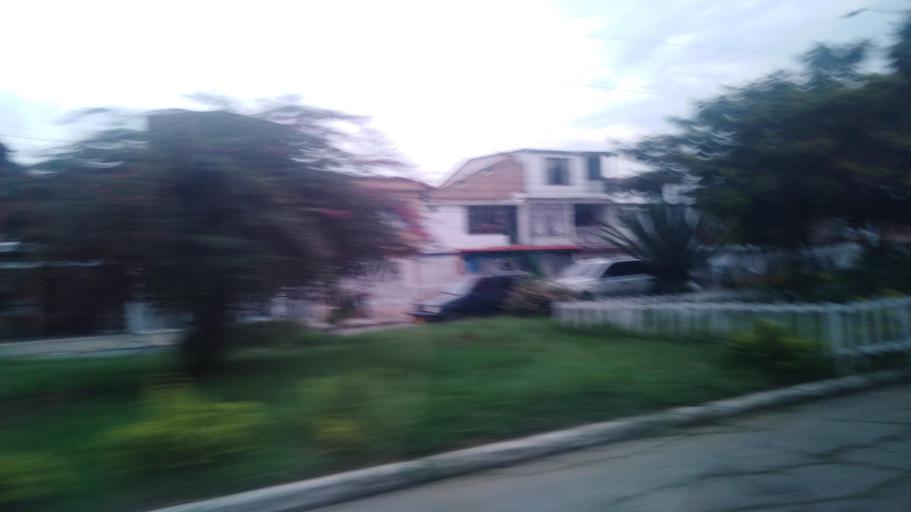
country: CO
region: Valle del Cauca
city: Cali
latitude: 3.4145
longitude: -76.5163
